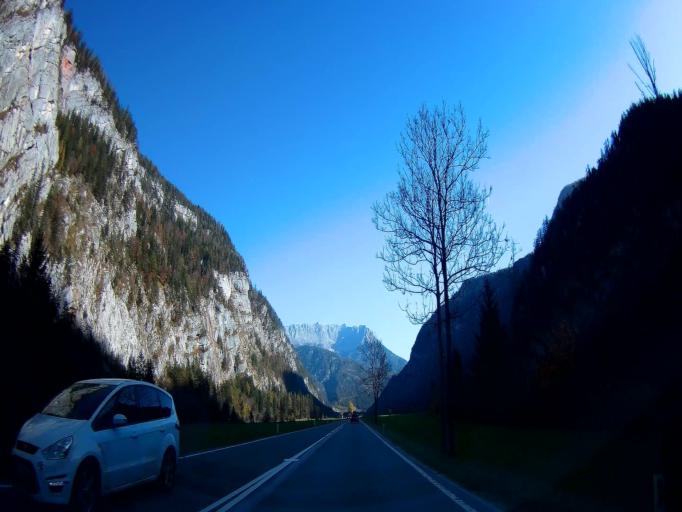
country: AT
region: Salzburg
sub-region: Politischer Bezirk Zell am See
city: Leogang
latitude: 47.5028
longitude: 12.7817
